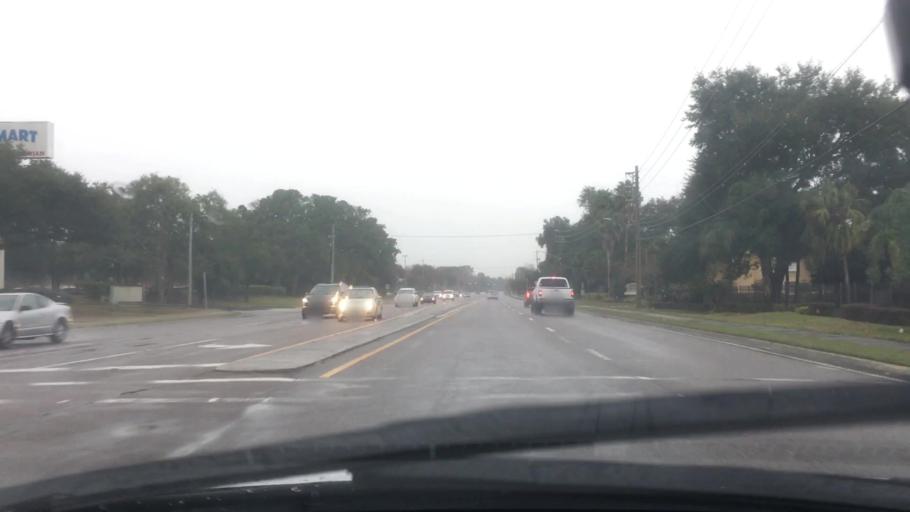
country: US
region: Florida
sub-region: Duval County
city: Jacksonville
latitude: 30.3264
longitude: -81.5469
